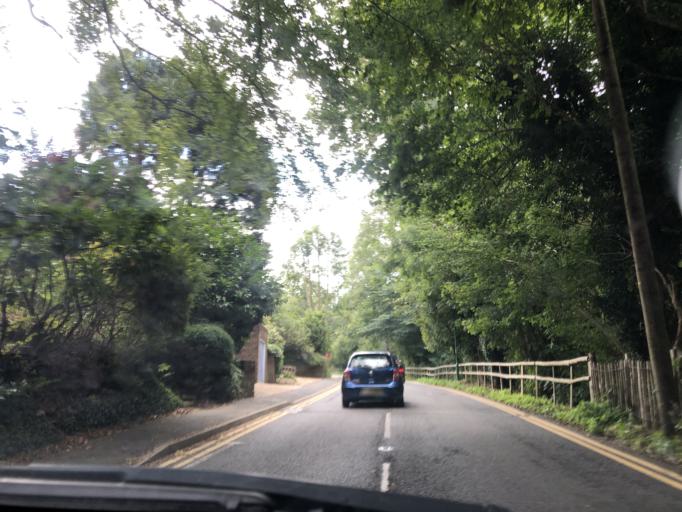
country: GB
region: England
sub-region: Kent
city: Westerham
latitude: 51.2638
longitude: 0.0779
